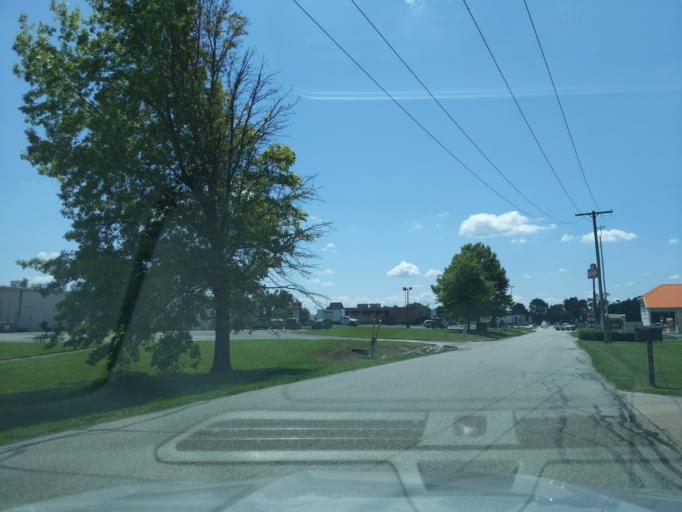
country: US
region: Indiana
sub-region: Decatur County
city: Greensburg
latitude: 39.3564
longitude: -85.4844
